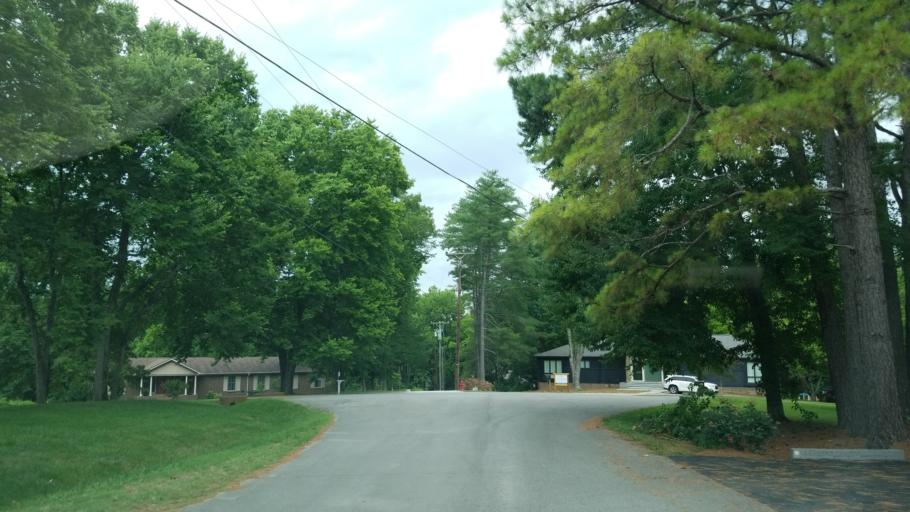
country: US
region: Tennessee
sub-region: Davidson County
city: Forest Hills
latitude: 36.0378
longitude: -86.8336
